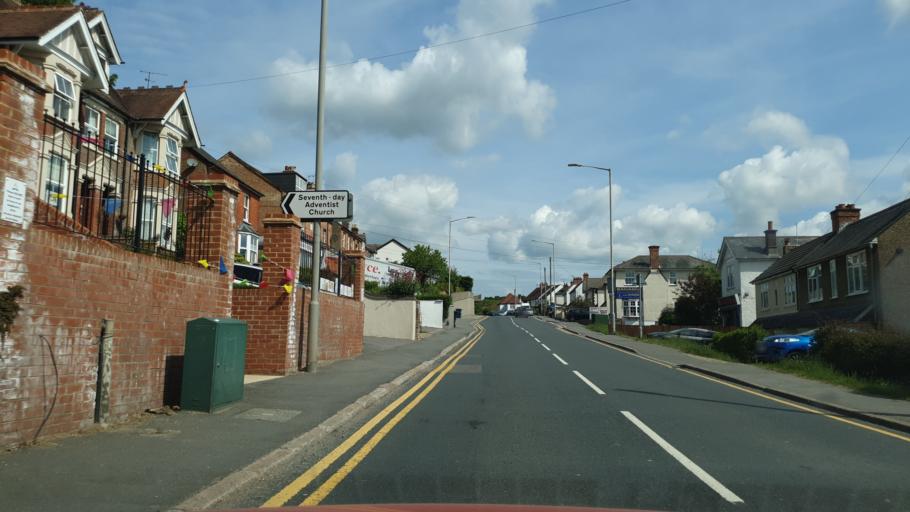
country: GB
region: England
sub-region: Buckinghamshire
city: High Wycombe
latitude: 51.6339
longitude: -0.7843
